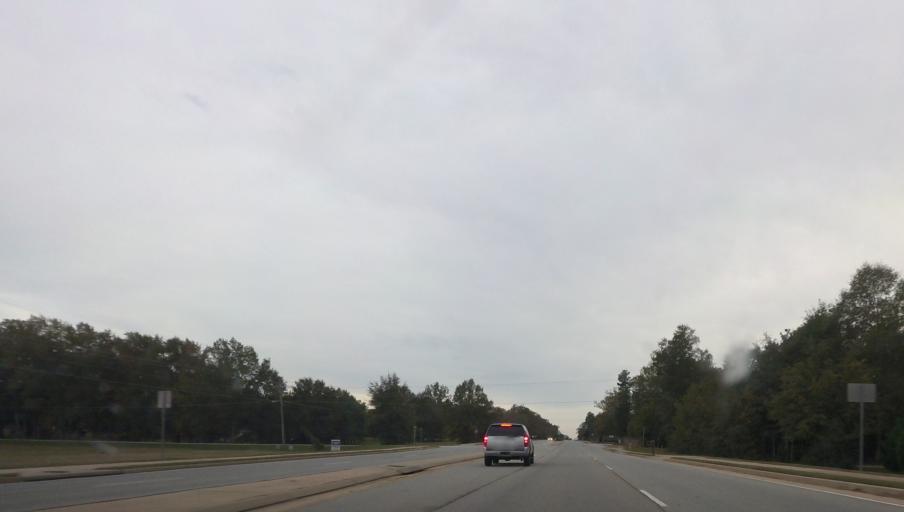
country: US
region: Georgia
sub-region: Houston County
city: Perry
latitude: 32.5294
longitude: -83.6624
